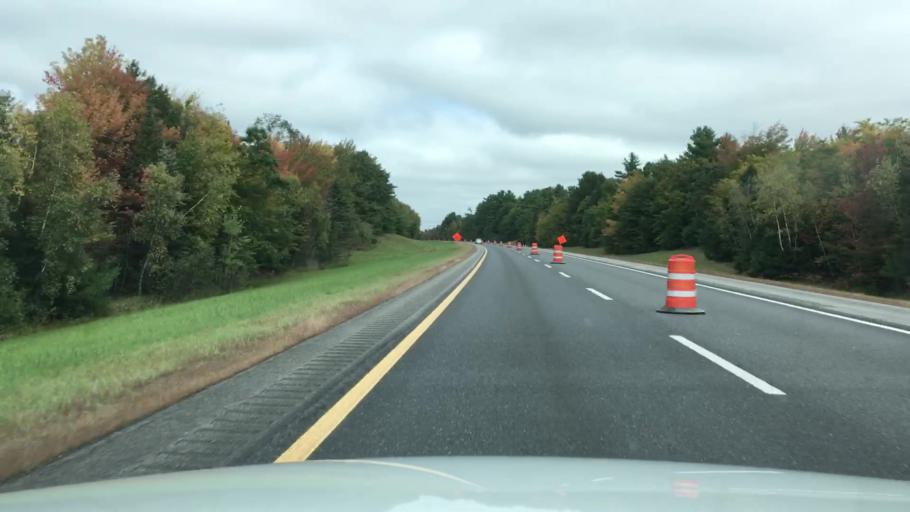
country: US
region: Maine
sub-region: Sagadahoc County
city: Richmond
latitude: 44.1199
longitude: -69.8519
